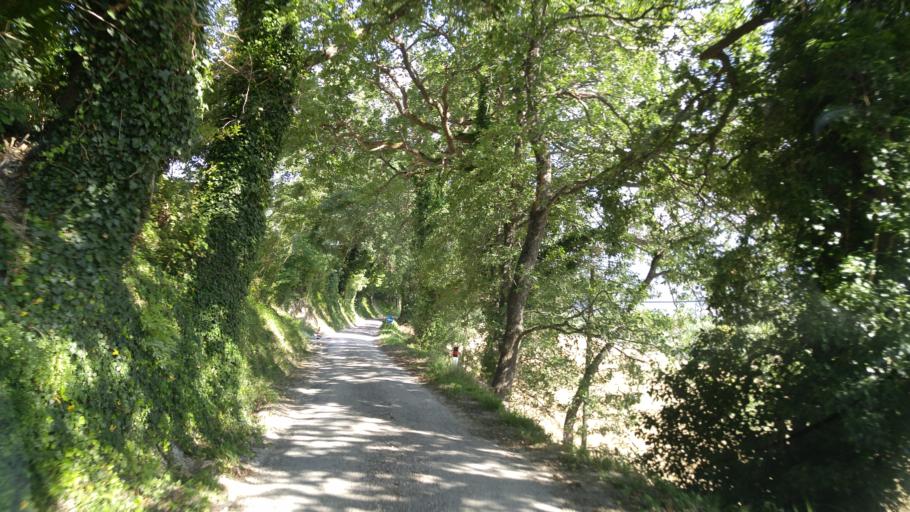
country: IT
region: The Marches
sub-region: Provincia di Pesaro e Urbino
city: Canavaccio
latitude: 43.6957
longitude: 12.7325
